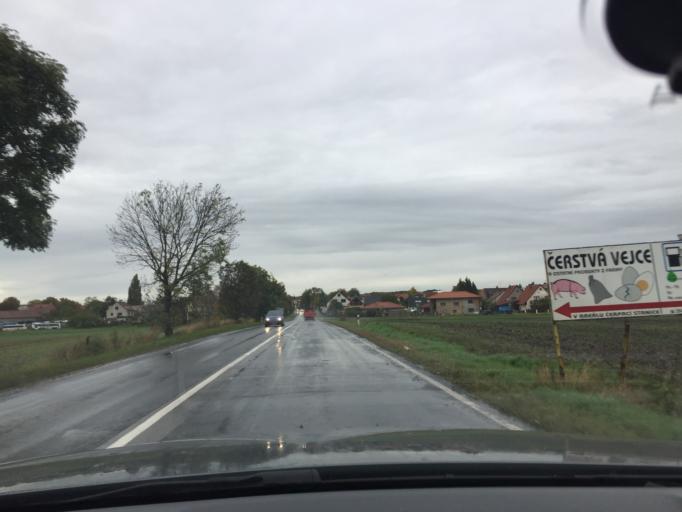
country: CZ
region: Central Bohemia
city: Klecany
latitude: 50.1972
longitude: 14.4361
